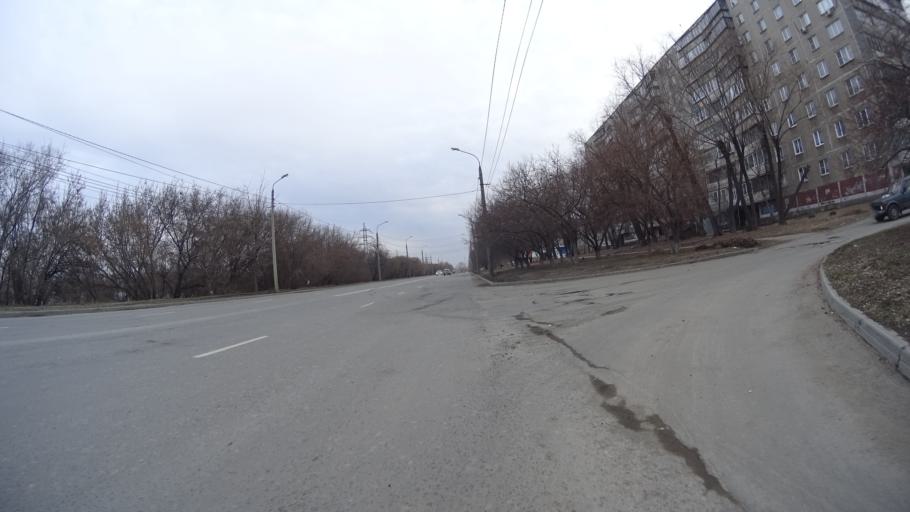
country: RU
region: Chelyabinsk
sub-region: Gorod Chelyabinsk
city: Chelyabinsk
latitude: 55.1838
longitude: 61.4855
